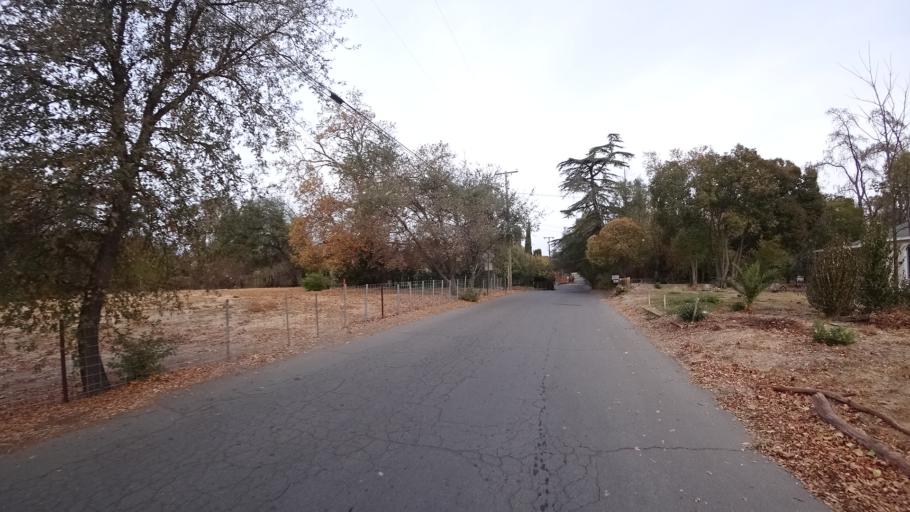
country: US
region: California
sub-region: Sacramento County
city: Citrus Heights
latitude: 38.7098
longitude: -121.2857
